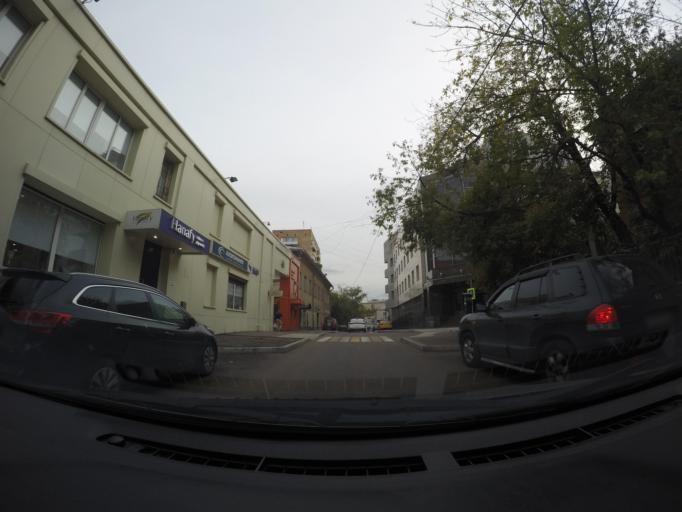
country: RU
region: Moscow
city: Lefortovo
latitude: 55.7838
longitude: 37.7087
